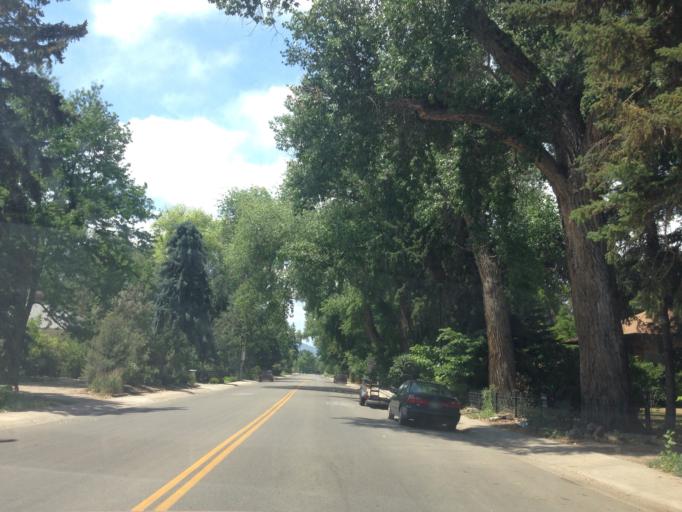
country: US
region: Colorado
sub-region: Larimer County
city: Fort Collins
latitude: 40.5742
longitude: -105.0631
